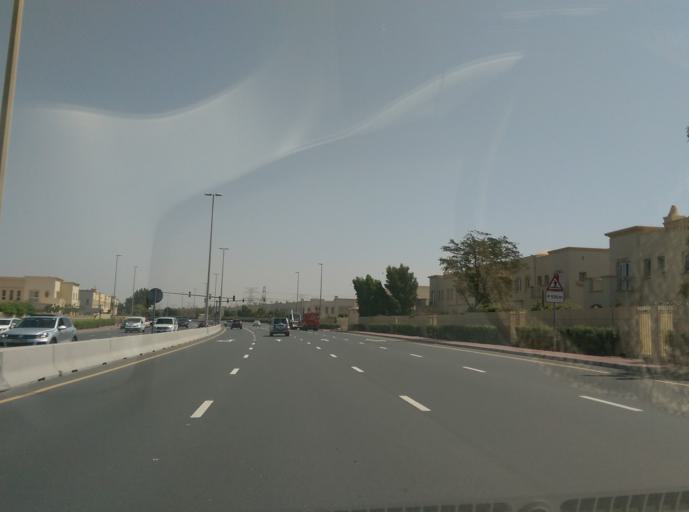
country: AE
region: Dubai
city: Dubai
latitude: 25.0606
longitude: 55.1847
